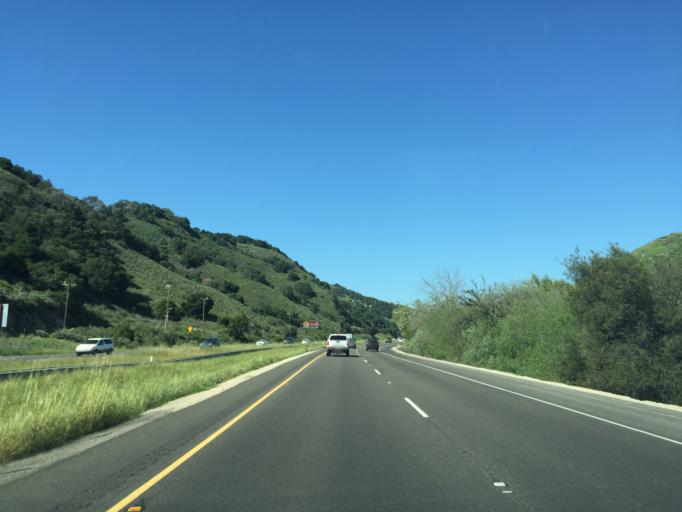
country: US
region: California
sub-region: San Luis Obispo County
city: Avila Beach
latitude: 35.2072
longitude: -120.6967
